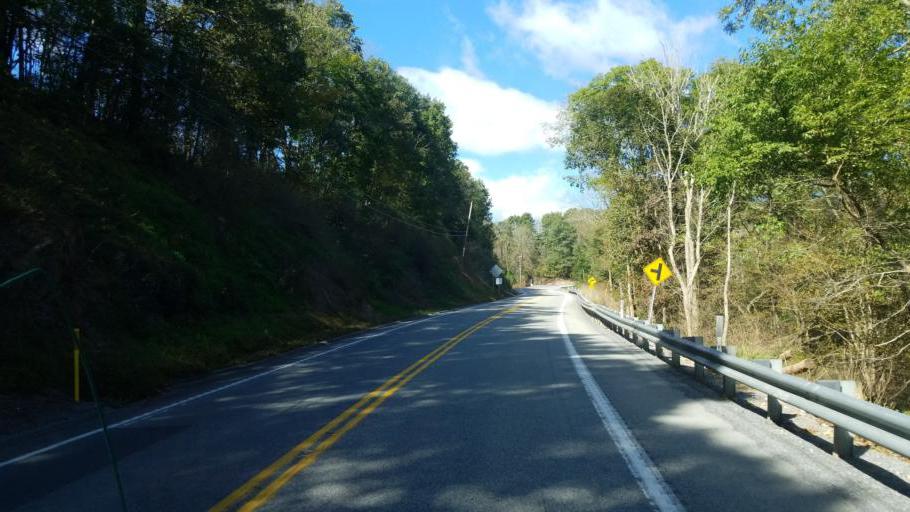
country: US
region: Pennsylvania
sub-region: Fulton County
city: McConnellsburg
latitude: 39.9814
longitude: -78.0450
